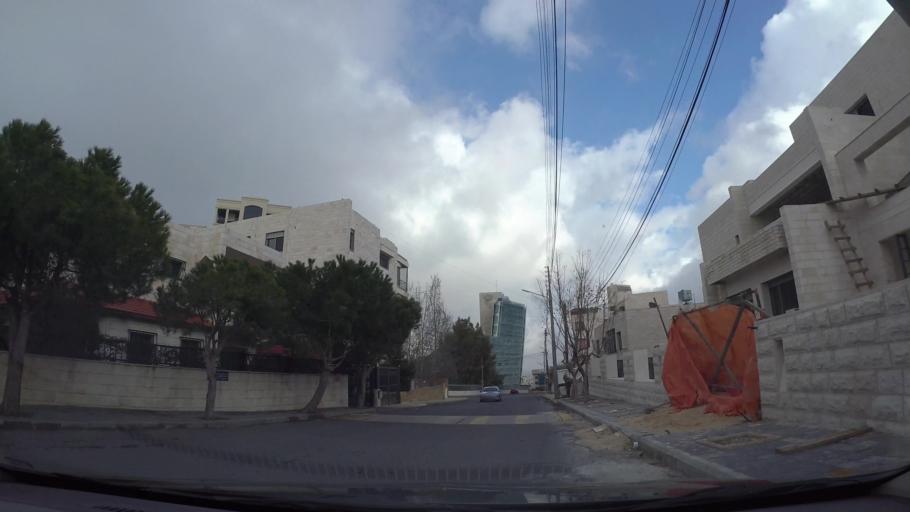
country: JO
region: Amman
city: Wadi as Sir
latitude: 31.9570
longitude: 35.8758
